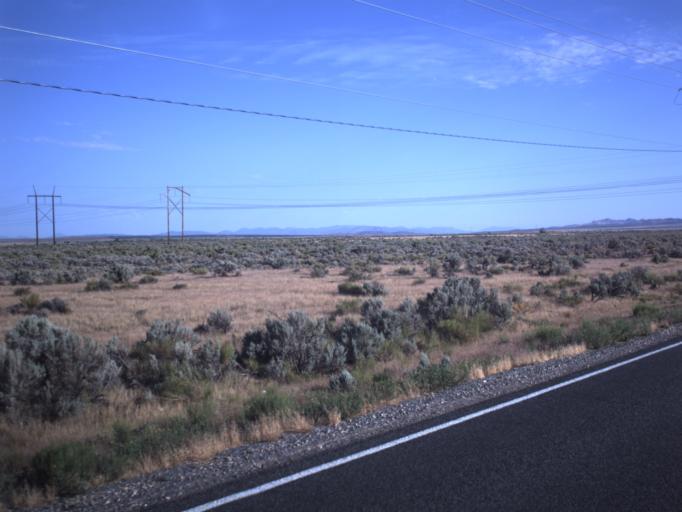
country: US
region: Utah
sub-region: Iron County
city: Enoch
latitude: 37.8002
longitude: -113.0506
